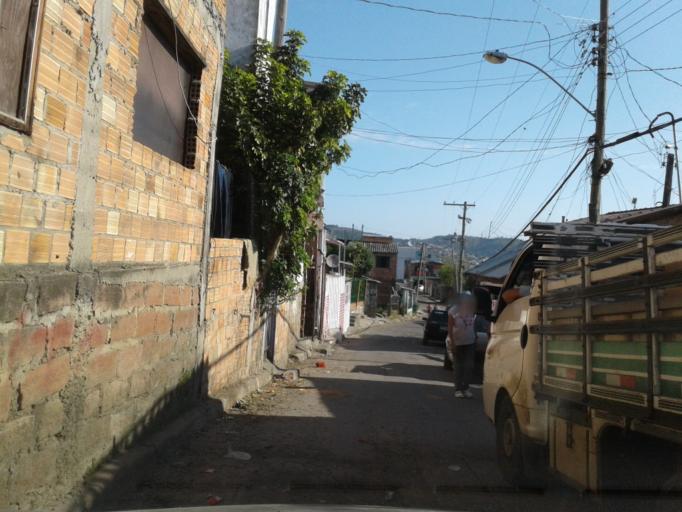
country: BR
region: Rio Grande do Sul
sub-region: Porto Alegre
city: Porto Alegre
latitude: -30.0471
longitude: -51.1505
